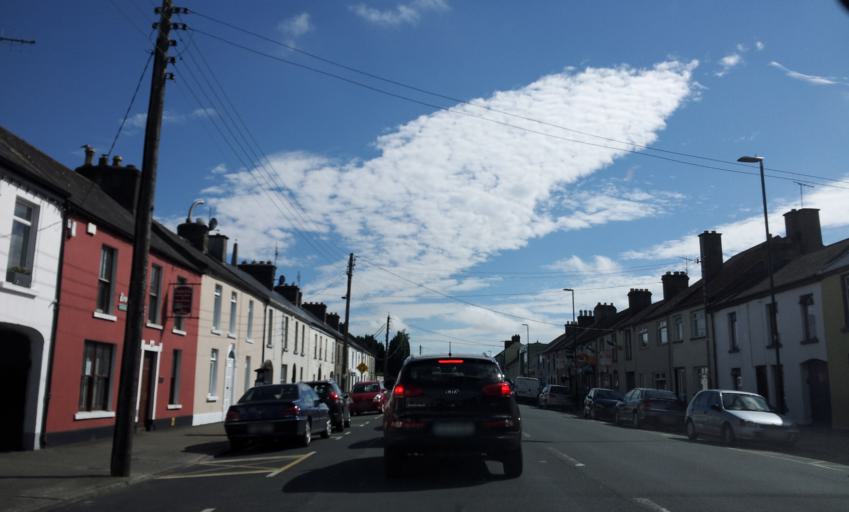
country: IE
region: Leinster
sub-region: Laois
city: Portlaoise
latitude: 53.0338
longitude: -7.3058
